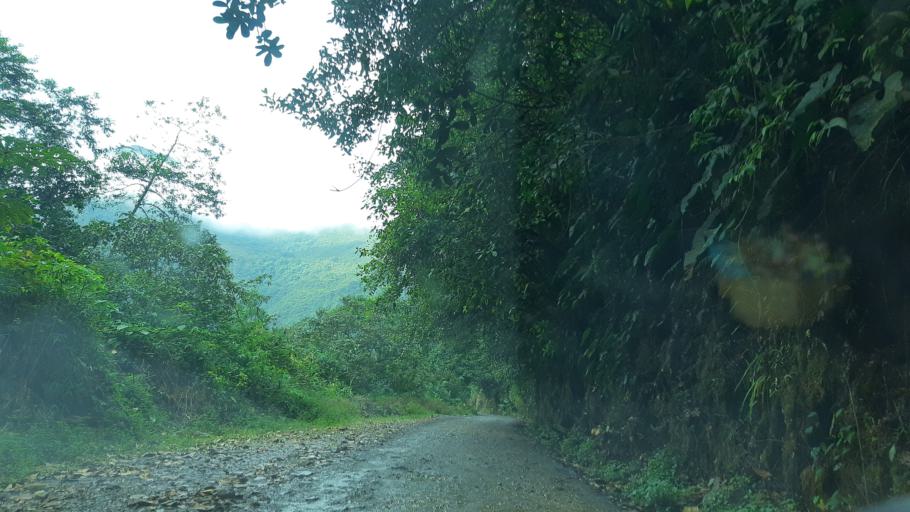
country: CO
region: Boyaca
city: Santa Maria
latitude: 4.8997
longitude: -73.3024
